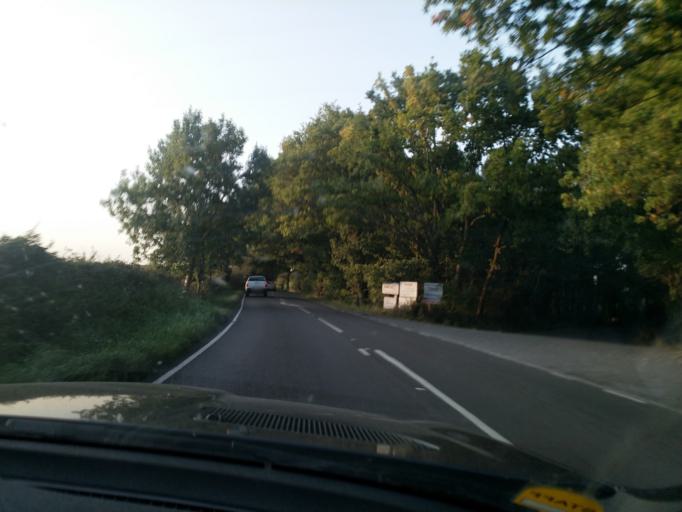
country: GB
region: England
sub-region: Kent
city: Queenborough
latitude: 51.3940
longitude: 0.7969
